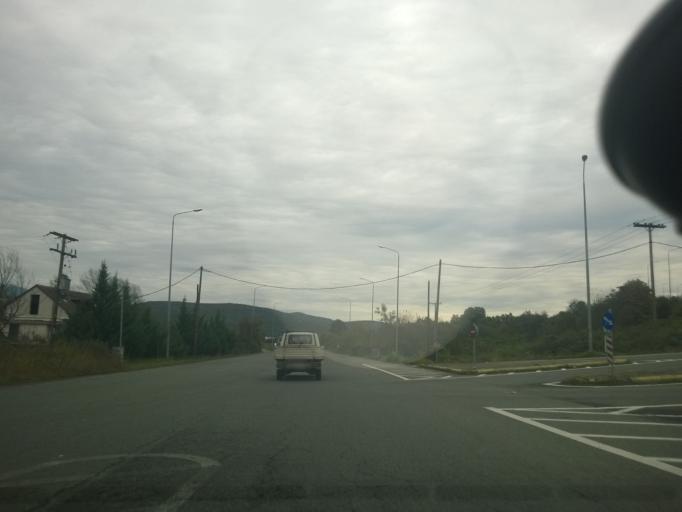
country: GR
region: Central Macedonia
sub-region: Nomos Pellis
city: Apsalos
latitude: 40.8875
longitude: 22.0697
